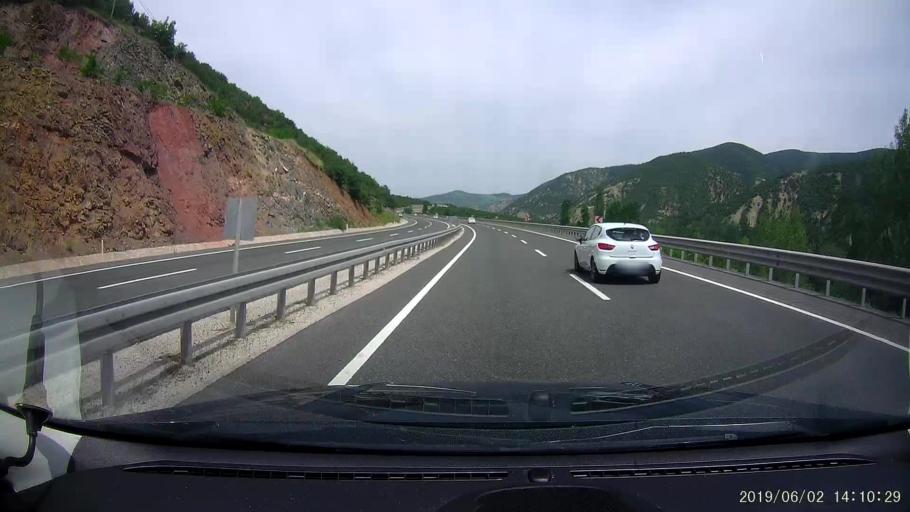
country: TR
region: Cankiri
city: Ilgaz
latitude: 40.9029
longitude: 33.7625
